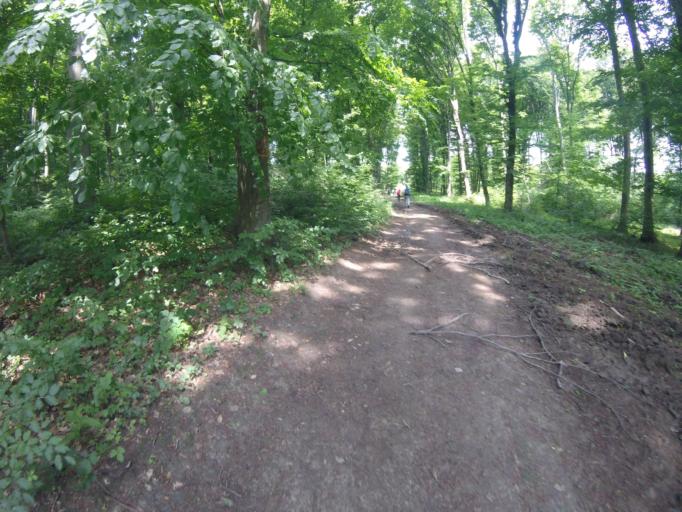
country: HU
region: Zala
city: Cserszegtomaj
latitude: 46.9084
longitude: 17.1930
